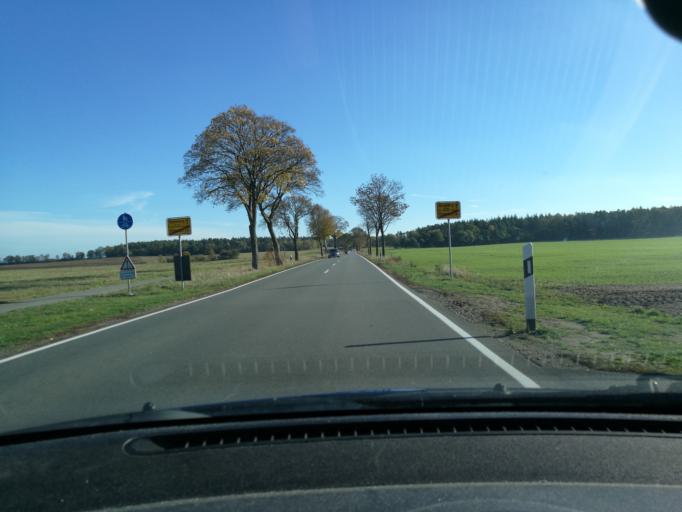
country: DE
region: Lower Saxony
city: Nahrendorf
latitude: 53.1568
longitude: 10.8154
